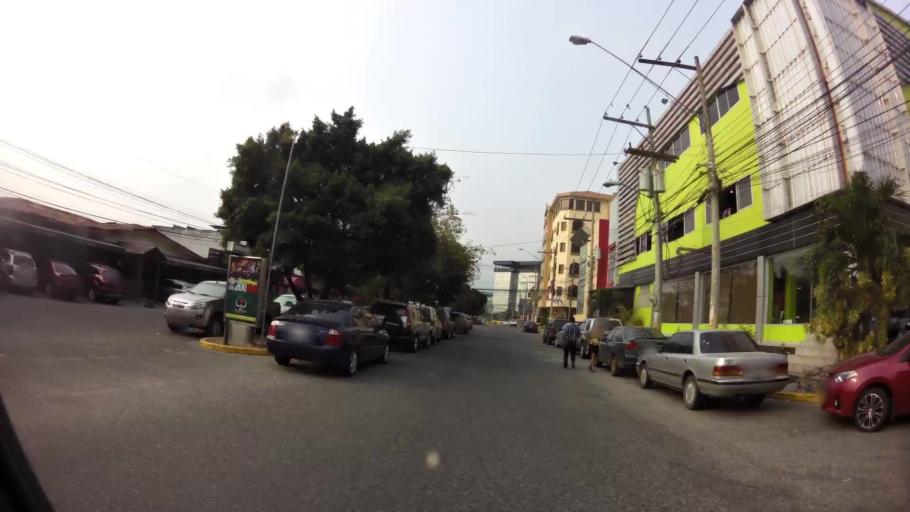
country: HN
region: Cortes
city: San Pedro Sula
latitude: 15.4998
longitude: -88.0359
